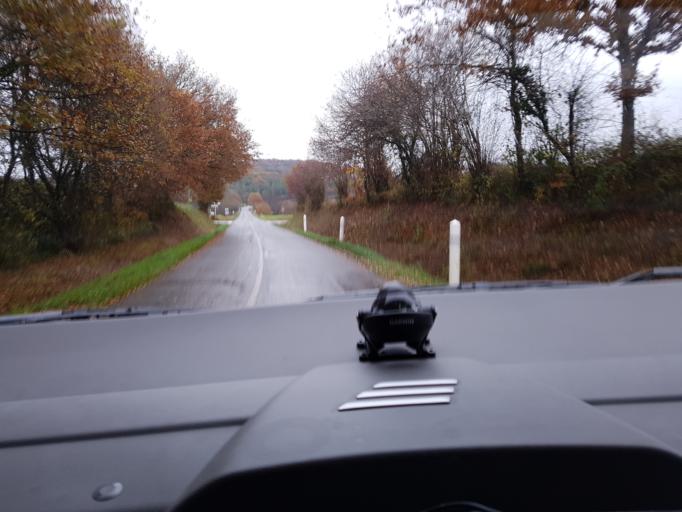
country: FR
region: Pays de la Loire
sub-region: Departement de la Mayenne
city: La Baconniere
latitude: 48.1891
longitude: -0.8543
